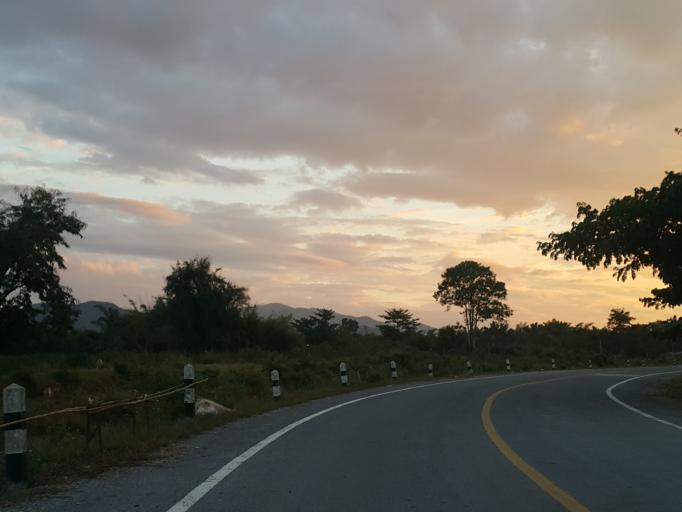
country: TH
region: Lampang
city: Mae Mo
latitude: 18.3822
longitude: 99.6097
